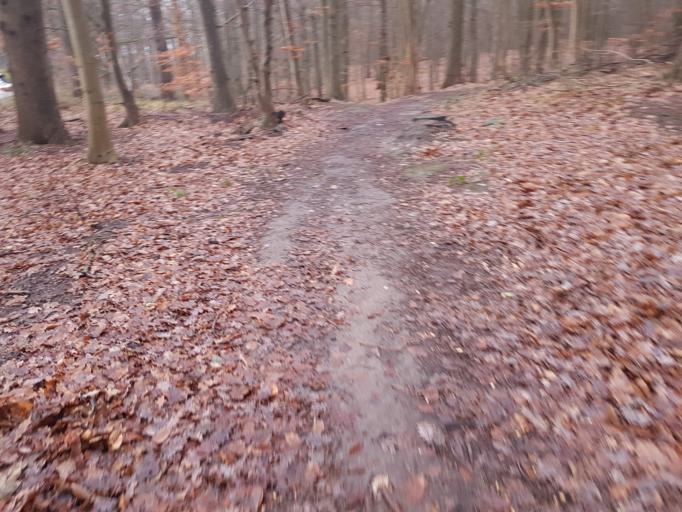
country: DE
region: Mecklenburg-Vorpommern
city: Ostseebad Binz
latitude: 54.3947
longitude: 13.6163
